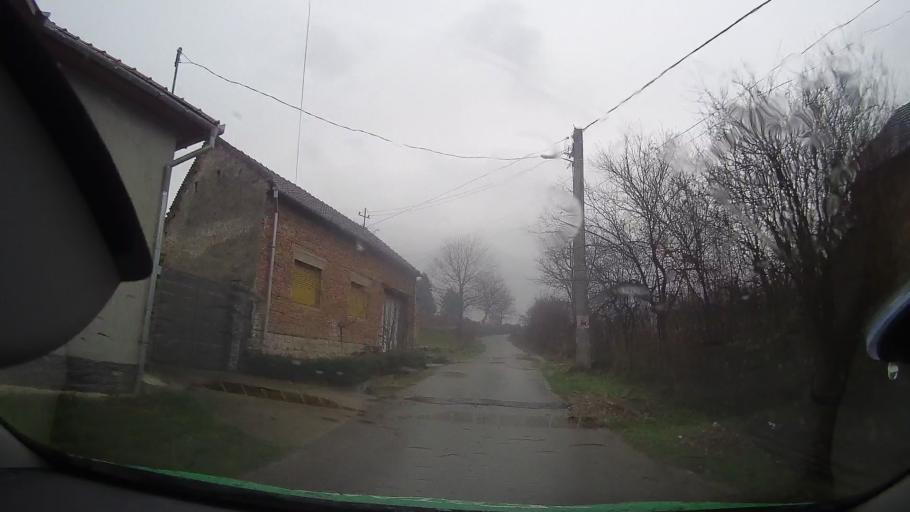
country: RO
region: Bihor
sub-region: Comuna Uileacu de Beius
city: Uileacu de Beius
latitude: 46.6865
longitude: 22.2198
